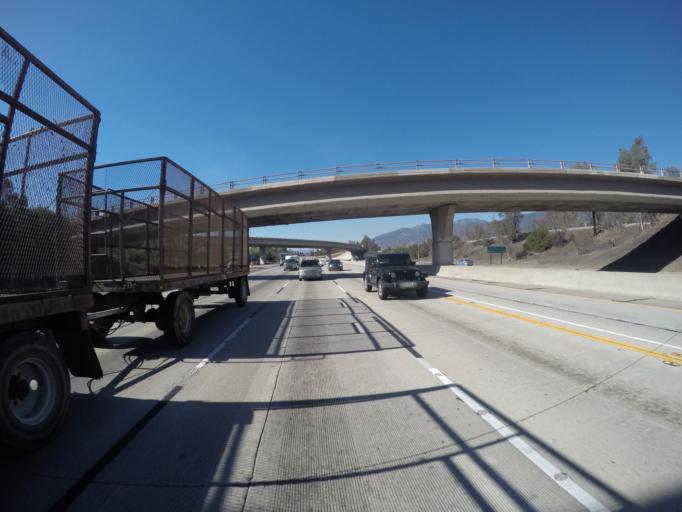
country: US
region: California
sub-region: Los Angeles County
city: Bradbury
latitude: 34.1345
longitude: -117.9582
